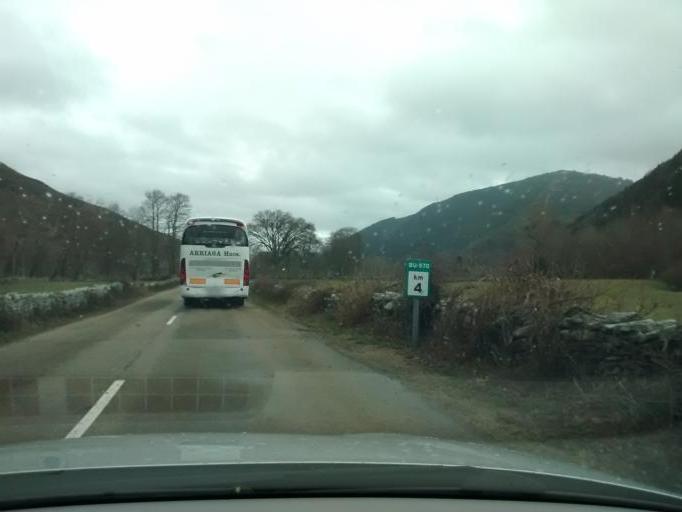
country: ES
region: Castille and Leon
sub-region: Provincia de Burgos
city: Espinosa de los Monteros
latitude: 43.1090
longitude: -3.5765
